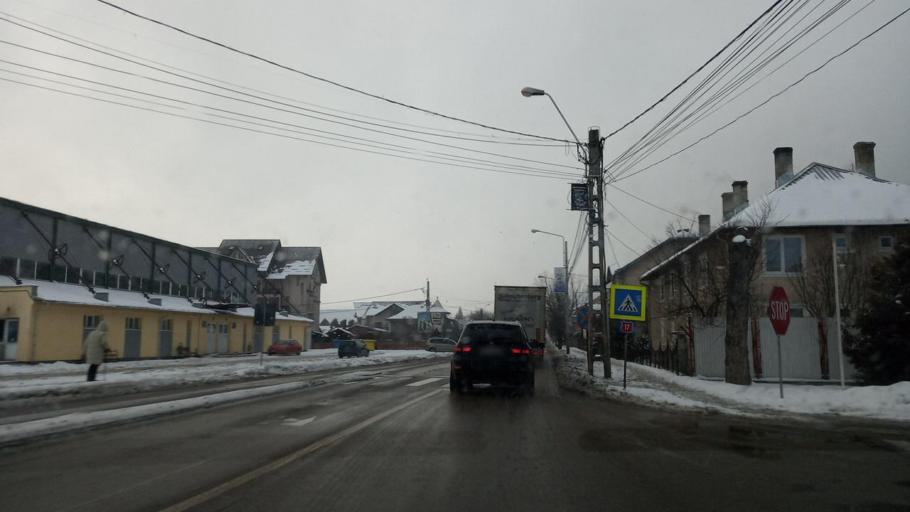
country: RO
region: Suceava
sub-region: Municipiul Vatra Dornei
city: Vatra Dornei
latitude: 47.3461
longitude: 25.3471
